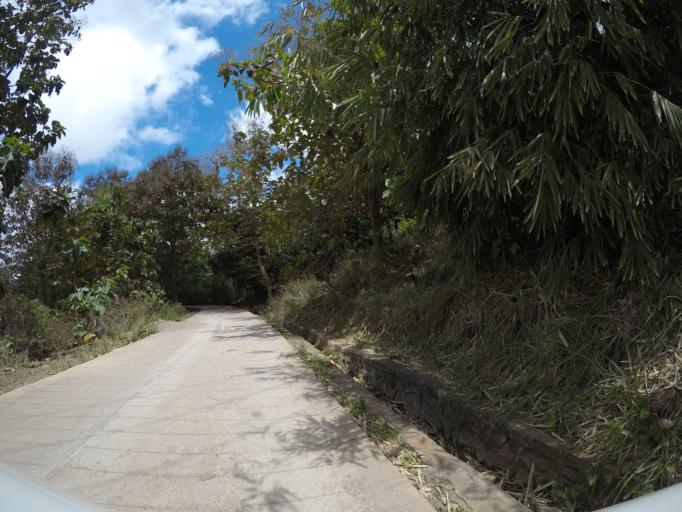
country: TL
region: Lautem
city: Lospalos
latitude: -8.5490
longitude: 126.8297
